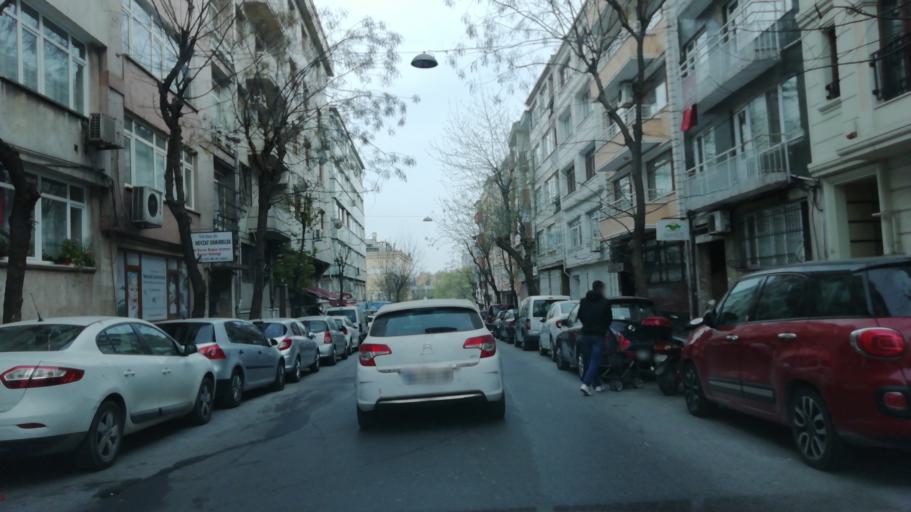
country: TR
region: Istanbul
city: Istanbul
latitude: 41.0152
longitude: 28.9505
